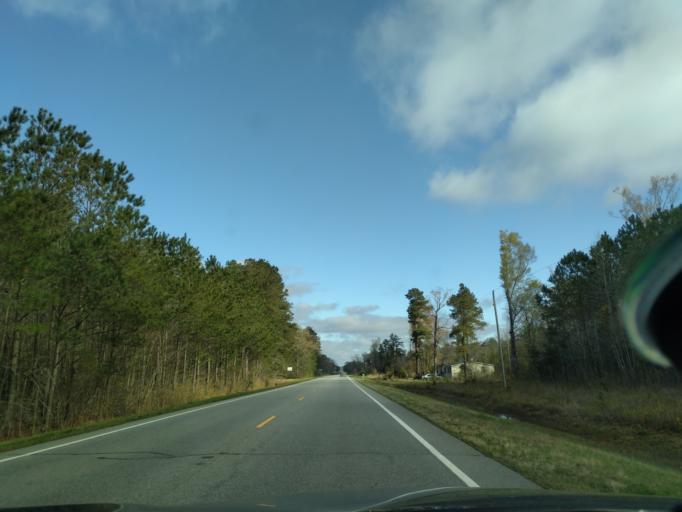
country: US
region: North Carolina
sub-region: Washington County
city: Plymouth
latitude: 36.0047
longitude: -76.7743
